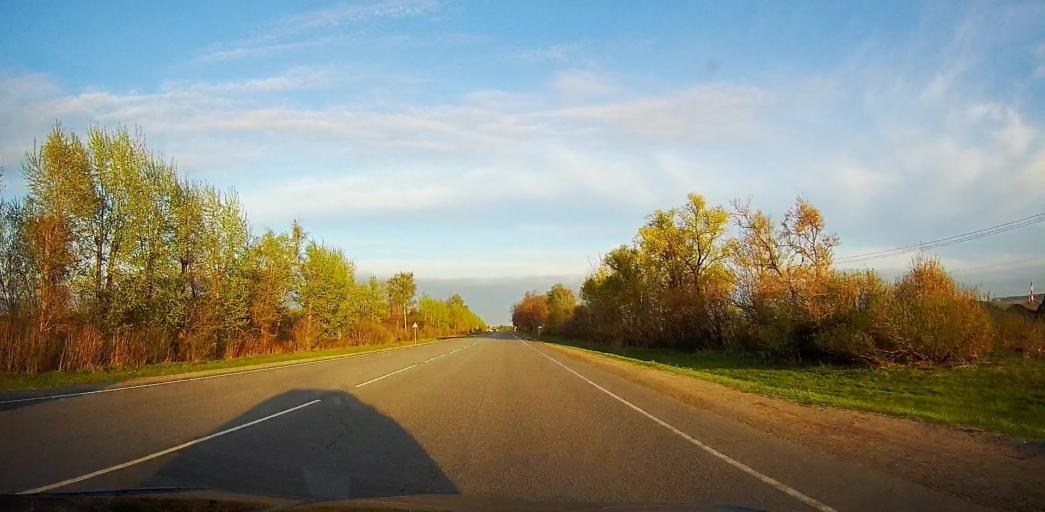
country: RU
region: Moskovskaya
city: Troitskoye
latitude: 55.2138
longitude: 38.5969
